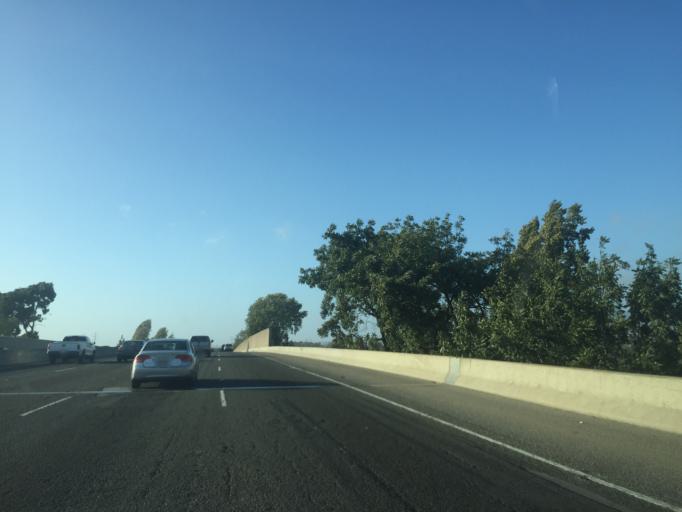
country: US
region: California
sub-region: Alameda County
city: San Leandro
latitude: 37.7259
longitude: -122.1833
